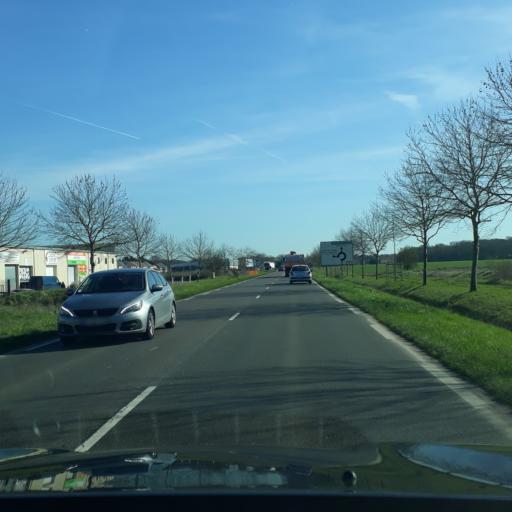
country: FR
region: Ile-de-France
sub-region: Departement de l'Essonne
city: Ballancourt-sur-Essonne
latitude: 48.5463
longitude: 2.4056
